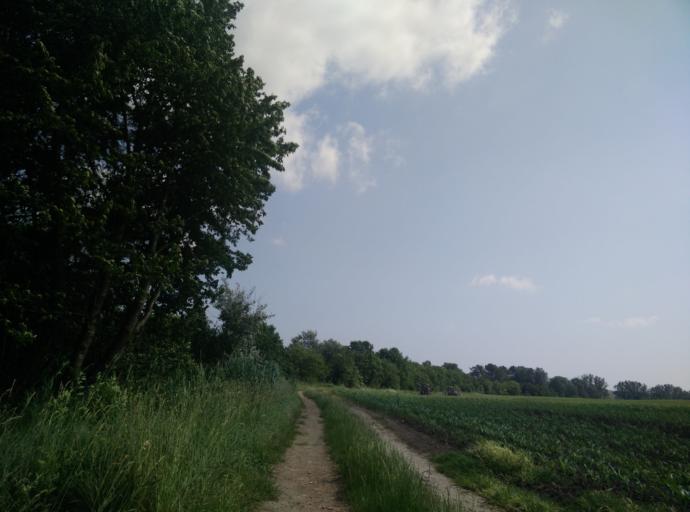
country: HU
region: Pest
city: Biatorbagy
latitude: 47.4766
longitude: 18.8047
